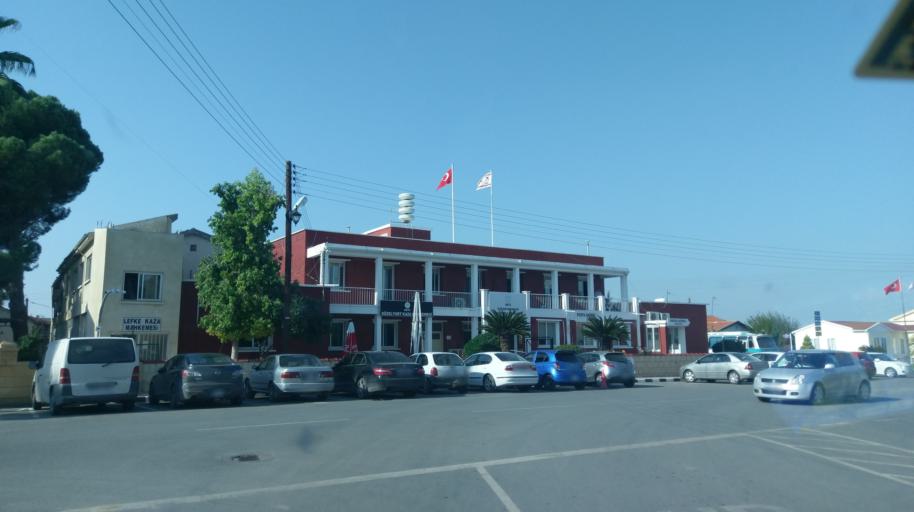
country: CY
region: Lefkosia
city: Morfou
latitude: 35.2008
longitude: 32.9897
